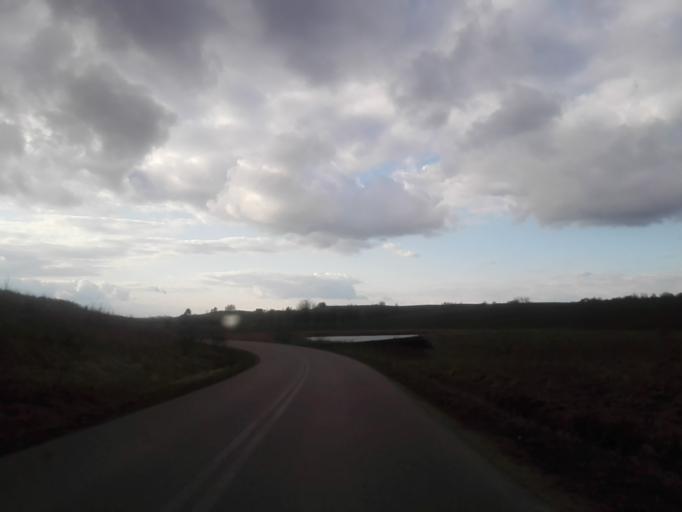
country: PL
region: Podlasie
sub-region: Suwalki
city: Suwalki
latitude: 54.1998
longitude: 22.9929
